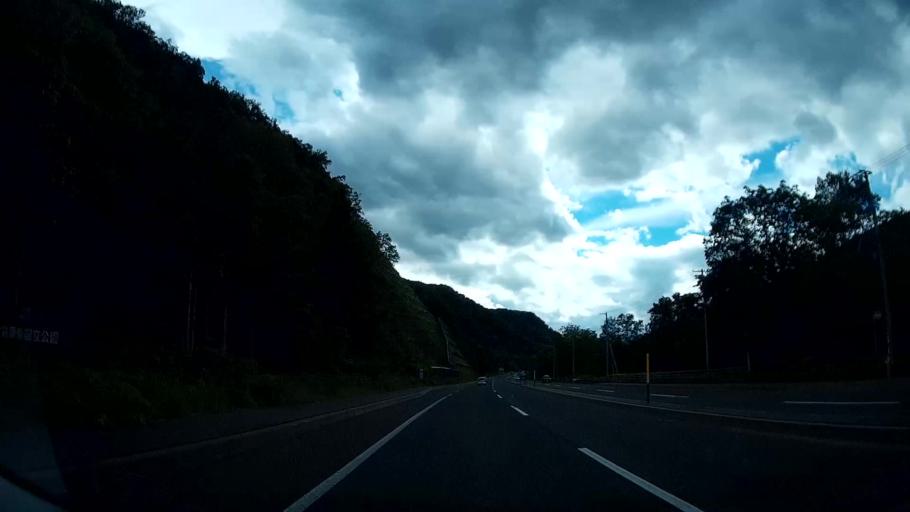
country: JP
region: Hokkaido
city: Sapporo
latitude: 42.9685
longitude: 141.2042
